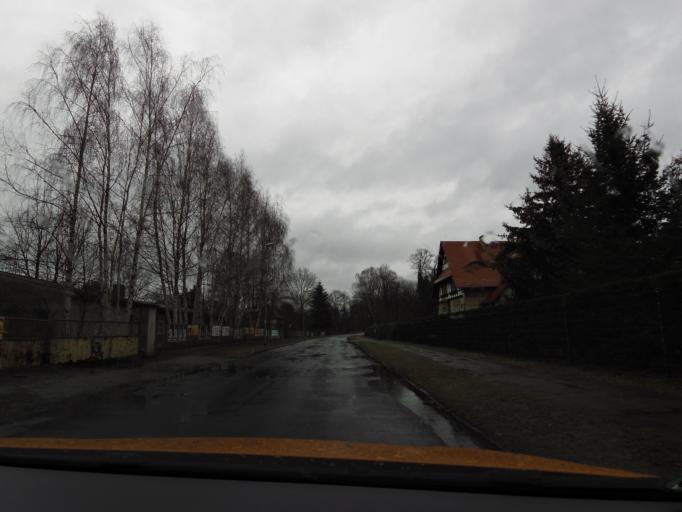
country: DE
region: Brandenburg
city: Am Mellensee
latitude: 52.1848
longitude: 13.4069
